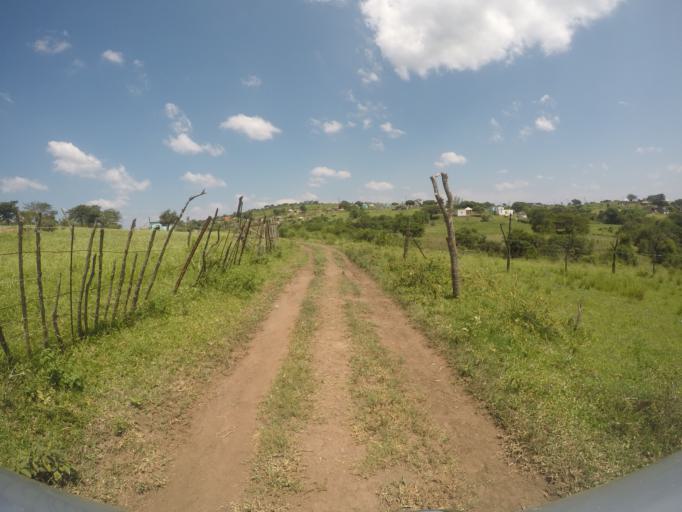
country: ZA
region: KwaZulu-Natal
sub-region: uThungulu District Municipality
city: Empangeni
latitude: -28.5975
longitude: 31.7361
